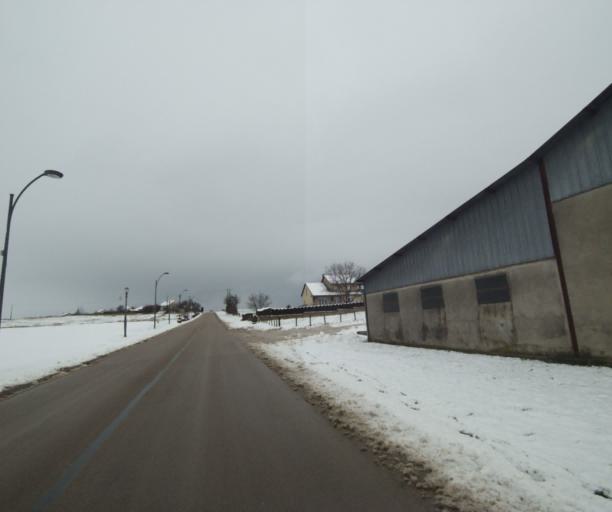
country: FR
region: Champagne-Ardenne
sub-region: Departement de la Haute-Marne
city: Laneuville-a-Remy
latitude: 48.4177
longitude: 4.8378
